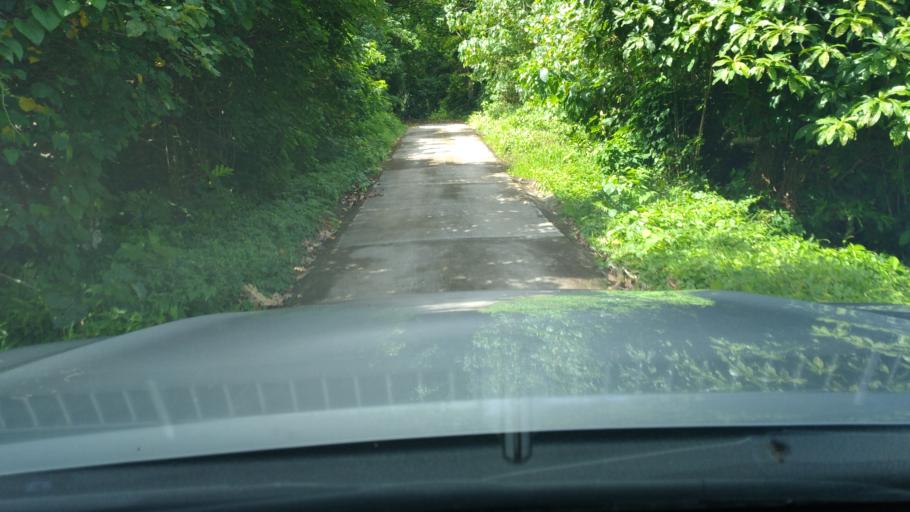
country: VU
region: Malampa
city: Lakatoro
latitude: -16.4330
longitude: 168.2328
